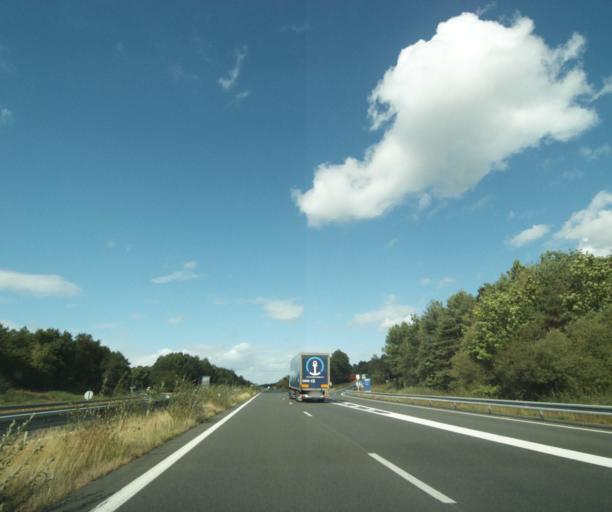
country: FR
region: Centre
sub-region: Departement du Loiret
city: Saint-Hilaire-Saint-Mesmin
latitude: 47.8066
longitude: 1.8529
